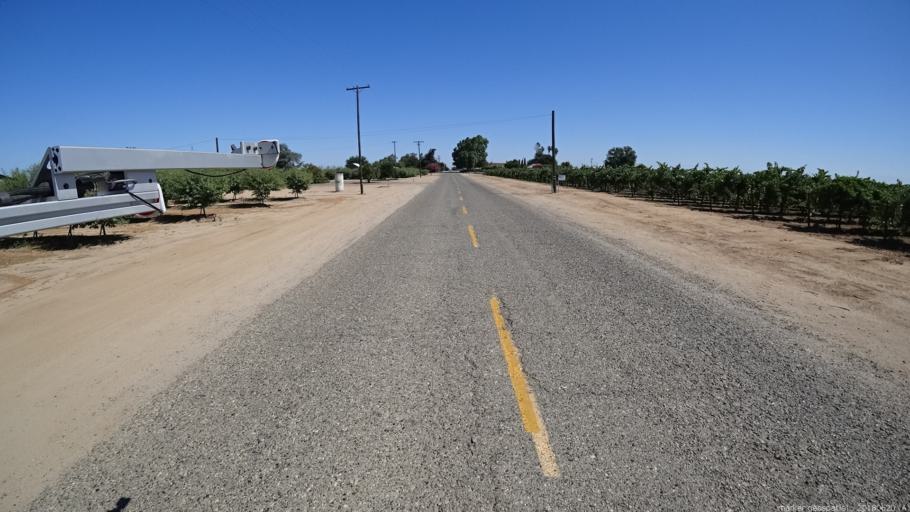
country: US
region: California
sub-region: Madera County
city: Parkwood
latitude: 36.8826
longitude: -120.0195
